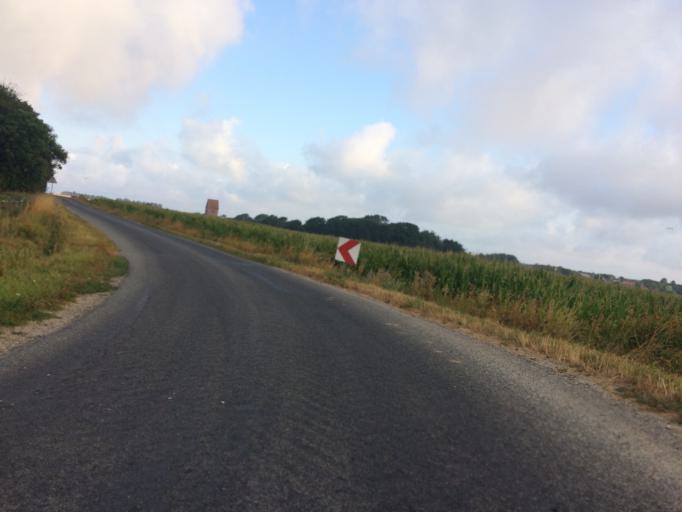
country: DK
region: Central Jutland
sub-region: Holstebro Kommune
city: Vinderup
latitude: 56.5947
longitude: 8.7387
